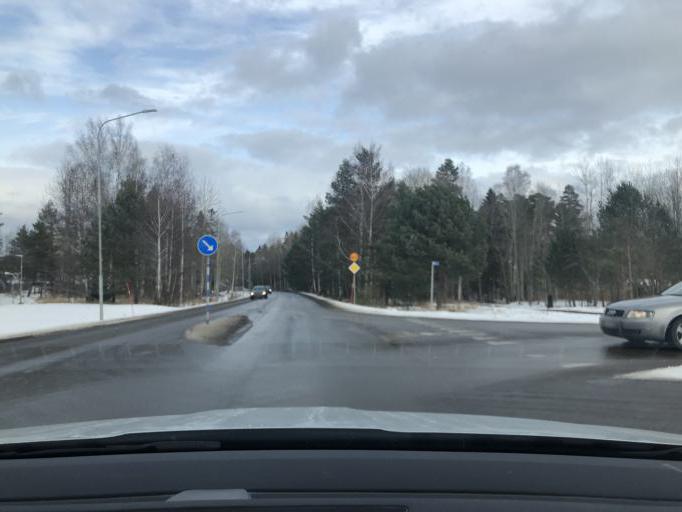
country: SE
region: OEstergoetland
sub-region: Motala Kommun
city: Motala
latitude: 58.5507
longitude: 15.0347
